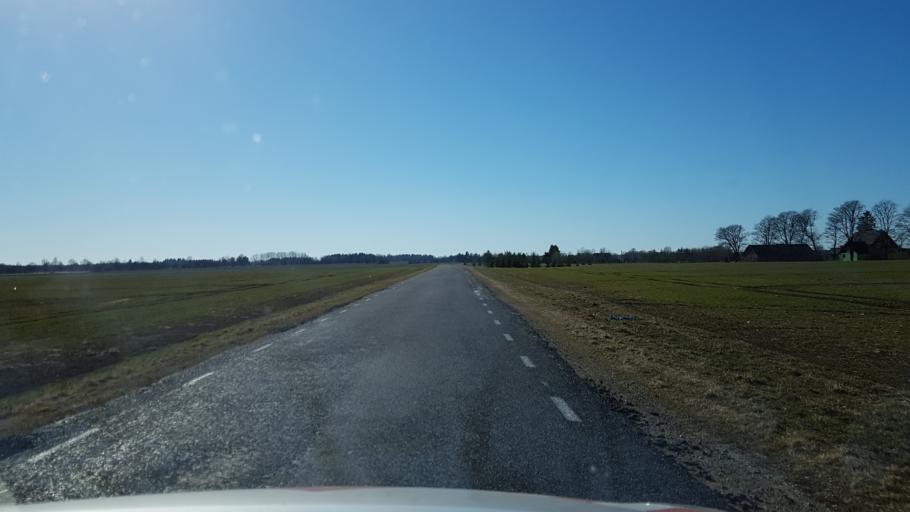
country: EE
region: Laeaene-Virumaa
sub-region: Haljala vald
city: Haljala
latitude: 59.4349
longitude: 26.2150
